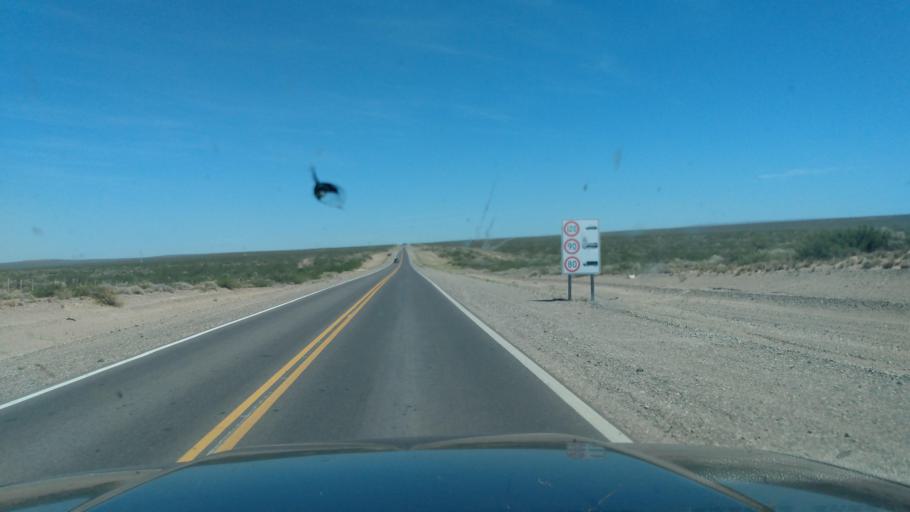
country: AR
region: Neuquen
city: Senillosa
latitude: -39.0727
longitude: -68.6036
